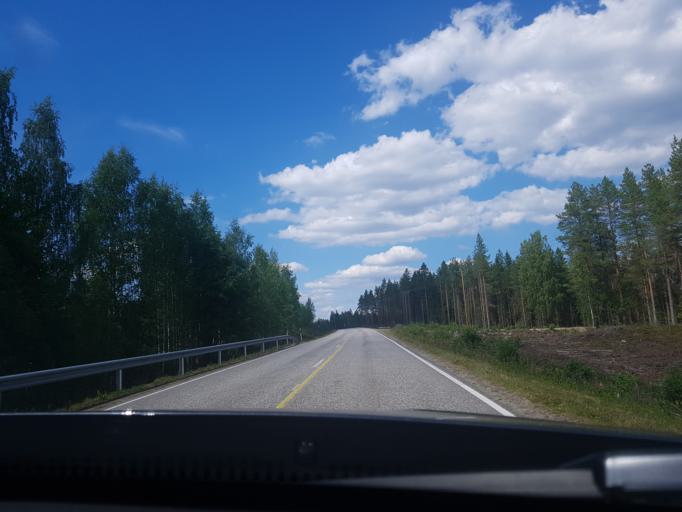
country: FI
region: Kainuu
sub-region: Kehys-Kainuu
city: Kuhmo
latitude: 64.2388
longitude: 29.8150
